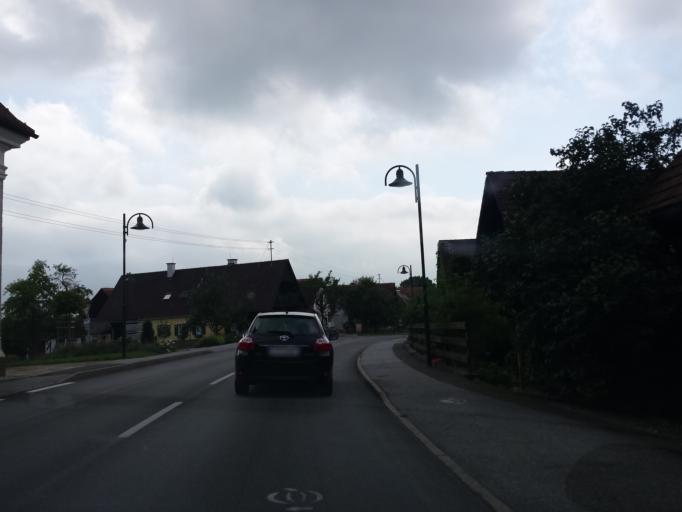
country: AT
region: Styria
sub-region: Politischer Bezirk Deutschlandsberg
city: Rassach
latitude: 46.8591
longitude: 15.2686
